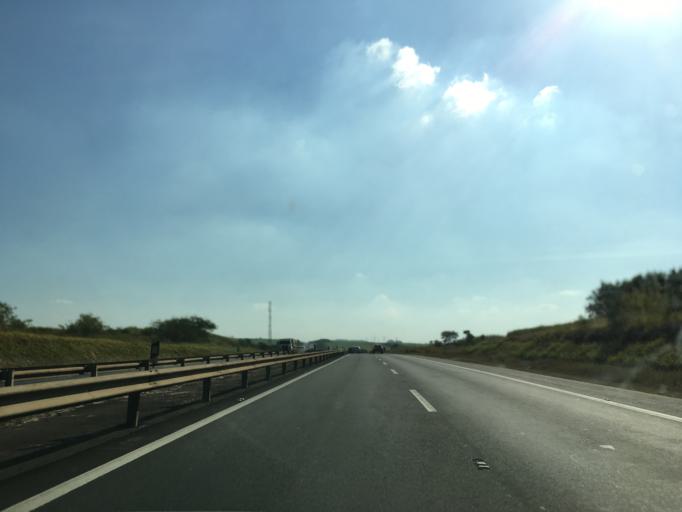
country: BR
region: Sao Paulo
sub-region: Piracicaba
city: Piracicaba
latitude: -22.7275
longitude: -47.5510
